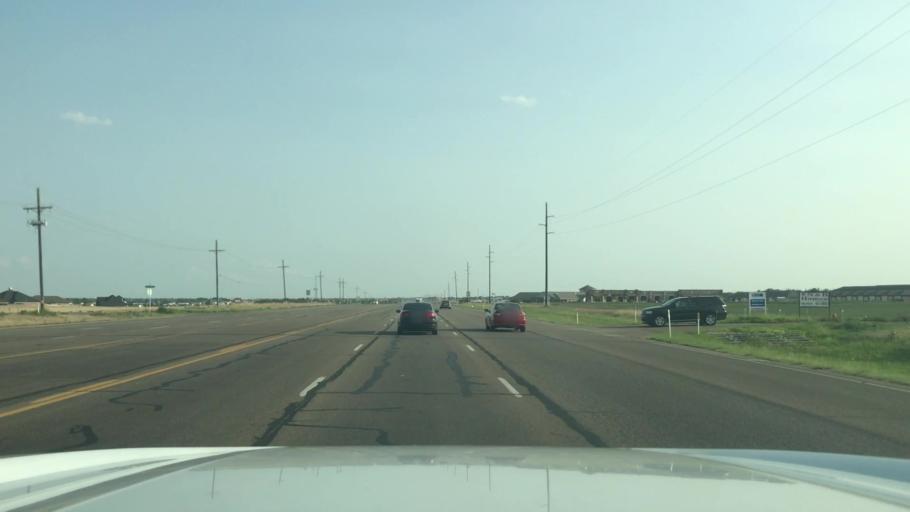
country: US
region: Texas
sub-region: Potter County
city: Amarillo
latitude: 35.1446
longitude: -101.9382
